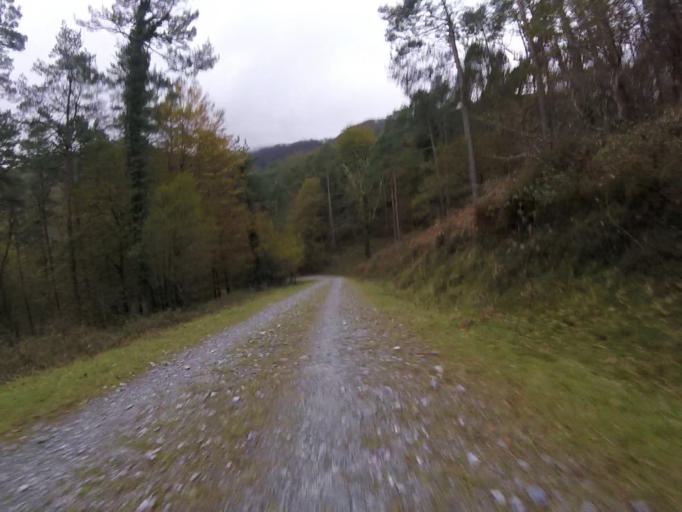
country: ES
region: Navarre
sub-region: Provincia de Navarra
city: Goizueta
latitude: 43.1792
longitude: -1.8073
